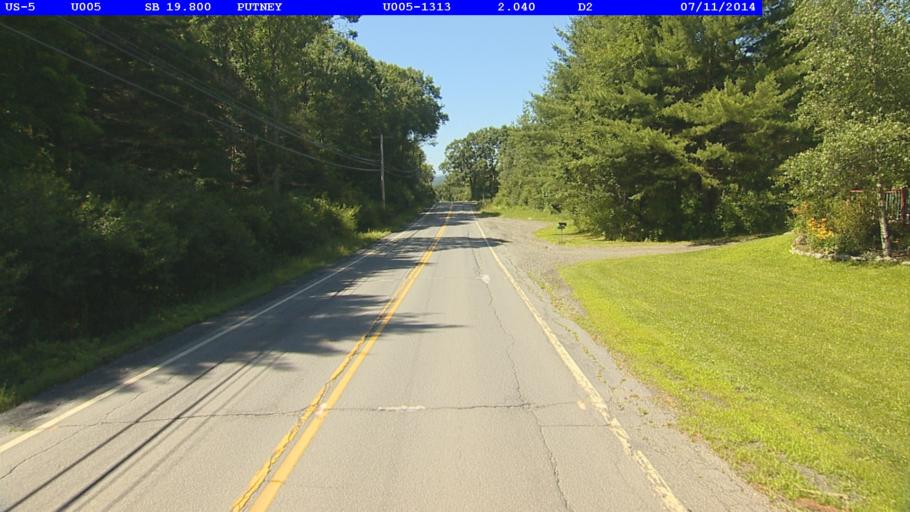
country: US
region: New Hampshire
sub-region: Cheshire County
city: Westmoreland
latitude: 42.9893
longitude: -72.5043
